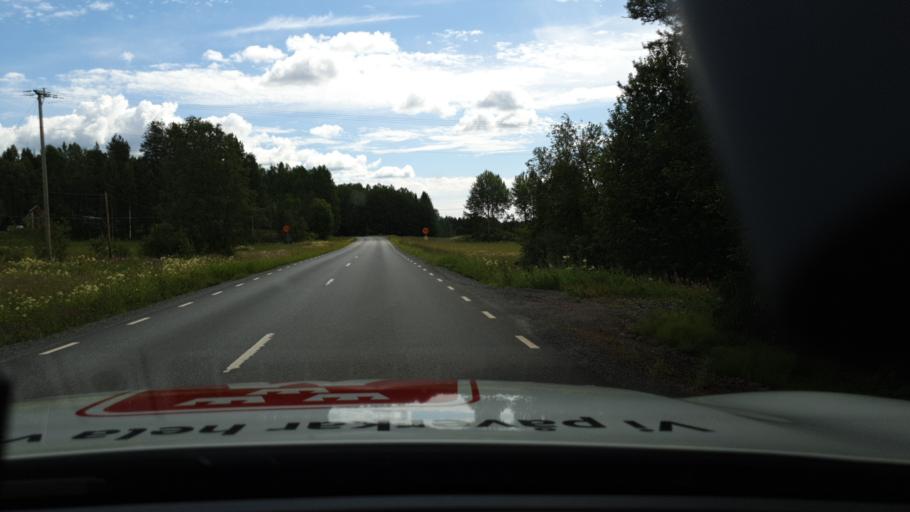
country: SE
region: Norrbotten
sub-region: Lulea Kommun
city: Sodra Sunderbyn
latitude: 65.8292
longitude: 21.9688
